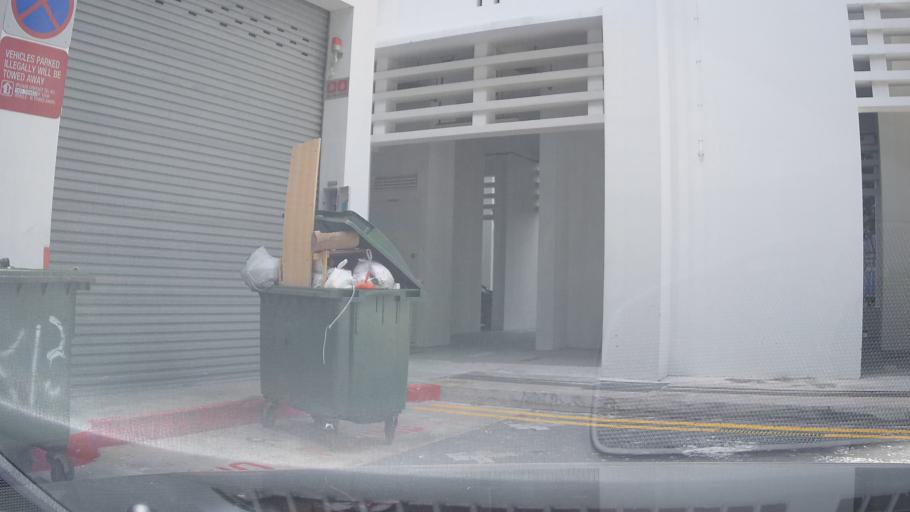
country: SG
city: Singapore
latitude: 1.3123
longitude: 103.8696
